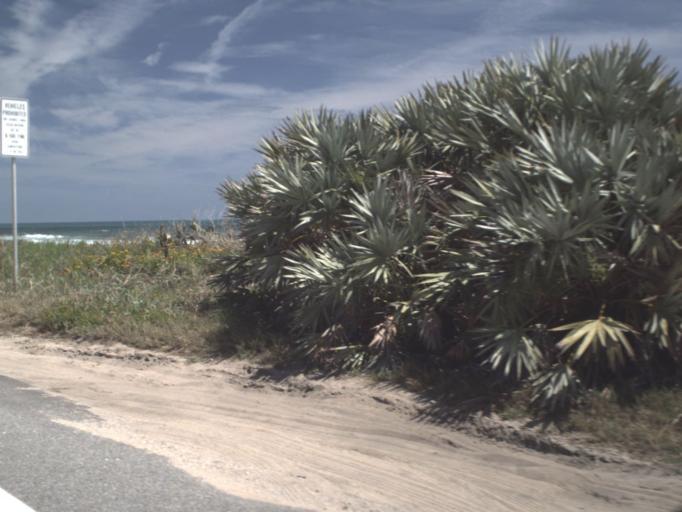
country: US
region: Florida
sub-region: Flagler County
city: Flagler Beach
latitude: 29.4452
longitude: -81.1107
